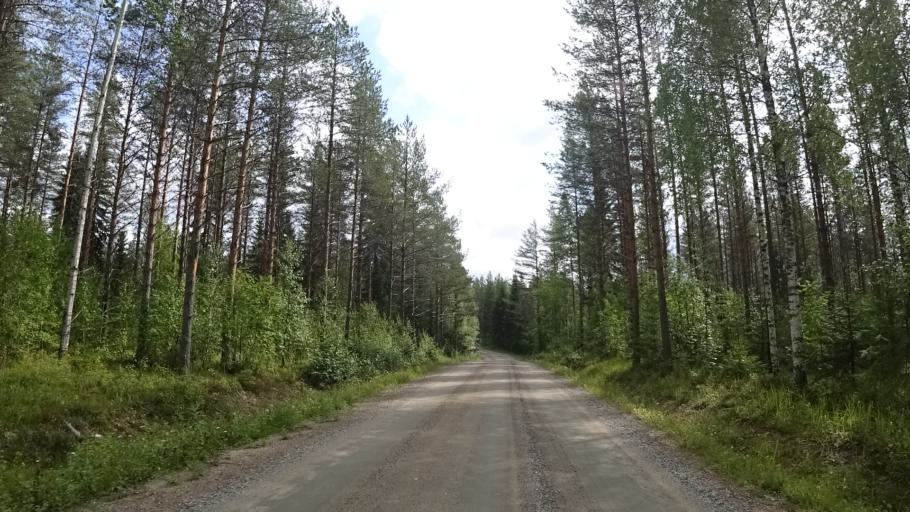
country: FI
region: North Karelia
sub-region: Joensuu
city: Ilomantsi
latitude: 62.9227
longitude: 31.3351
